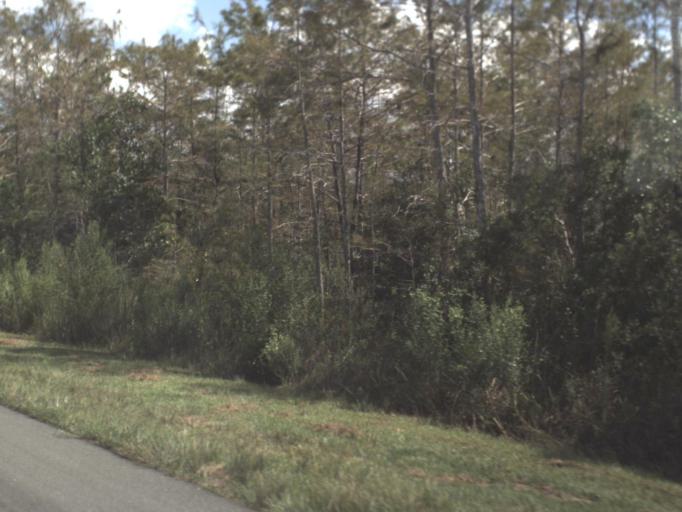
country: US
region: Florida
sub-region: Miami-Dade County
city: Kendall West
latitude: 25.8533
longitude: -80.9986
